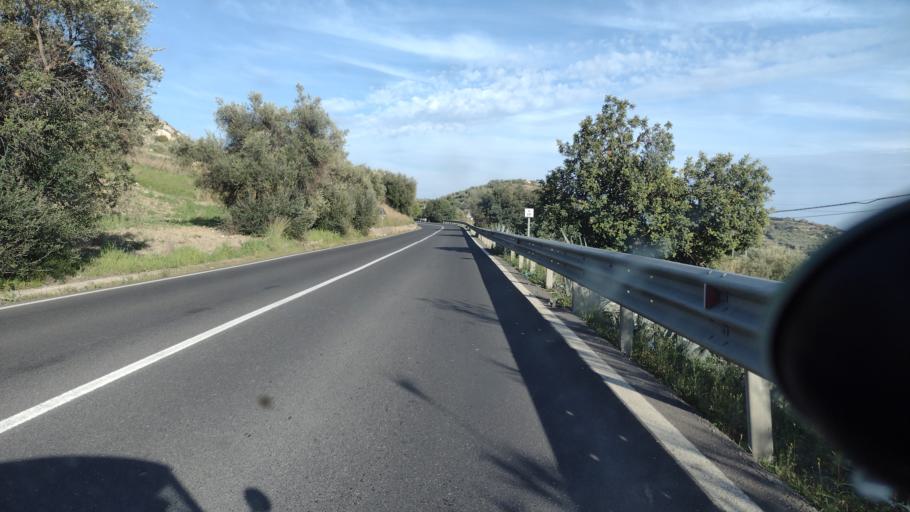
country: IT
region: Sicily
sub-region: Provincia di Siracusa
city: Noto
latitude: 36.8673
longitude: 15.0299
